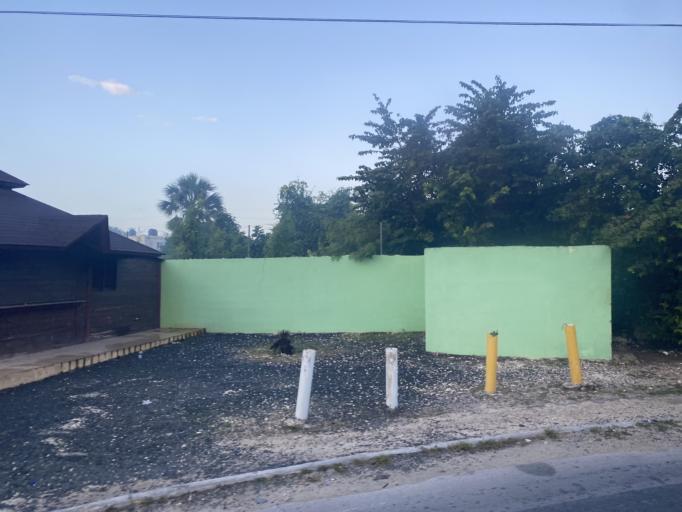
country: DO
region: San Juan
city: Punta Cana
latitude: 18.7192
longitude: -68.4743
